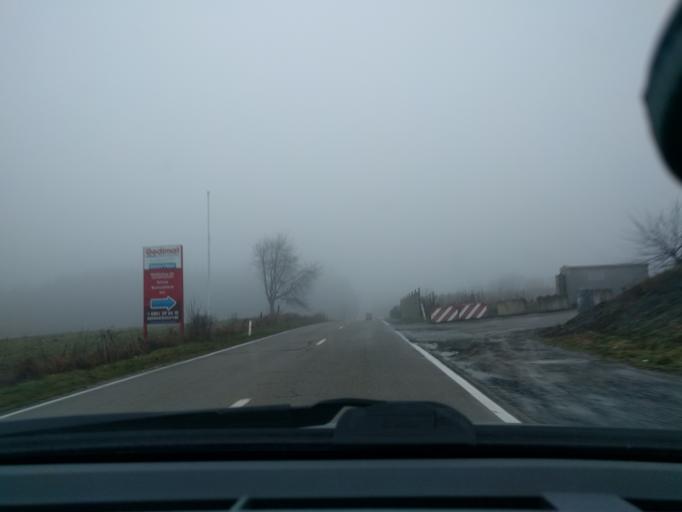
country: BE
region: Wallonia
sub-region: Province du Luxembourg
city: Gouvy
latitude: 50.2001
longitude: 5.9227
